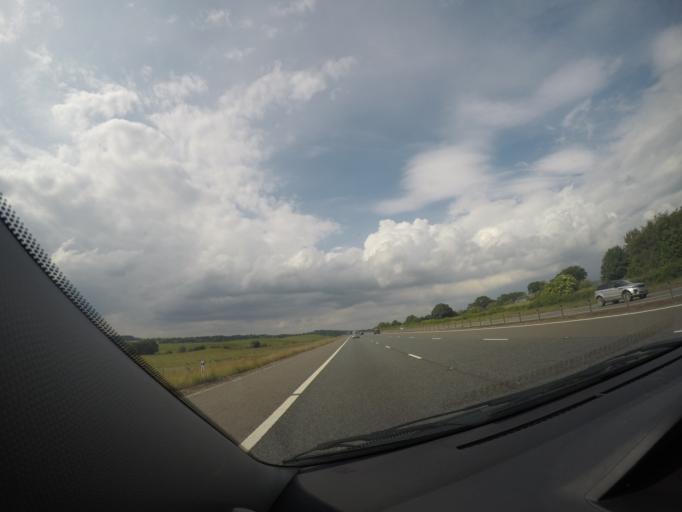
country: GB
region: Scotland
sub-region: Dumfries and Galloway
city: Lochmaben
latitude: 55.1969
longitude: -3.4104
